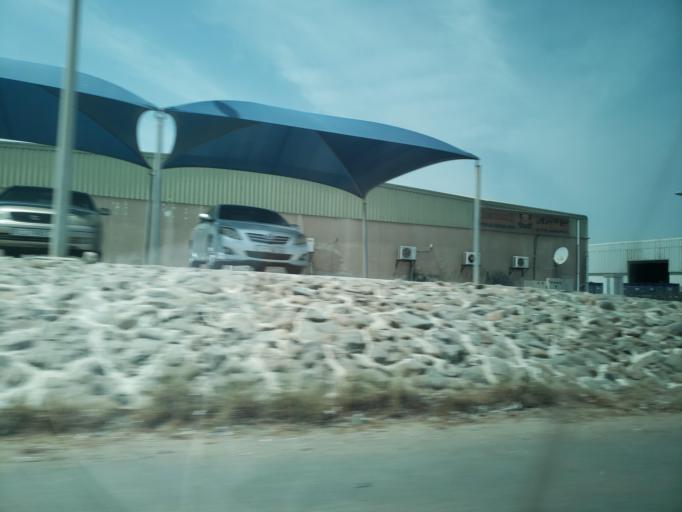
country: AE
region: Ash Shariqah
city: Sharjah
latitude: 25.3332
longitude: 55.4940
